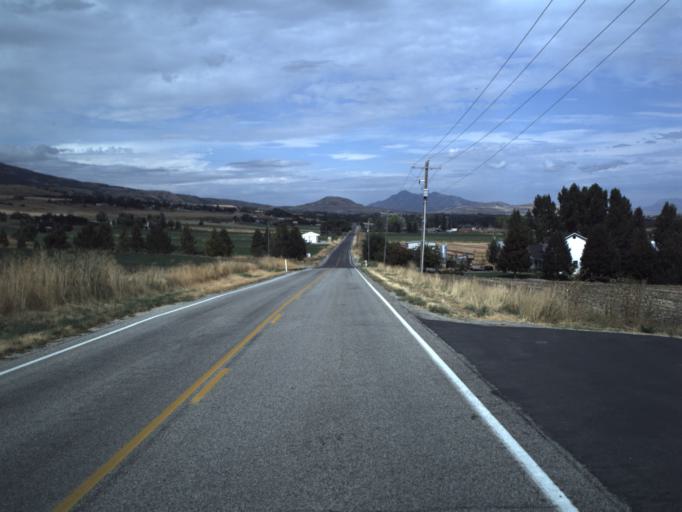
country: US
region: Utah
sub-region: Cache County
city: Wellsville
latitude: 41.6724
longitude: -111.9551
